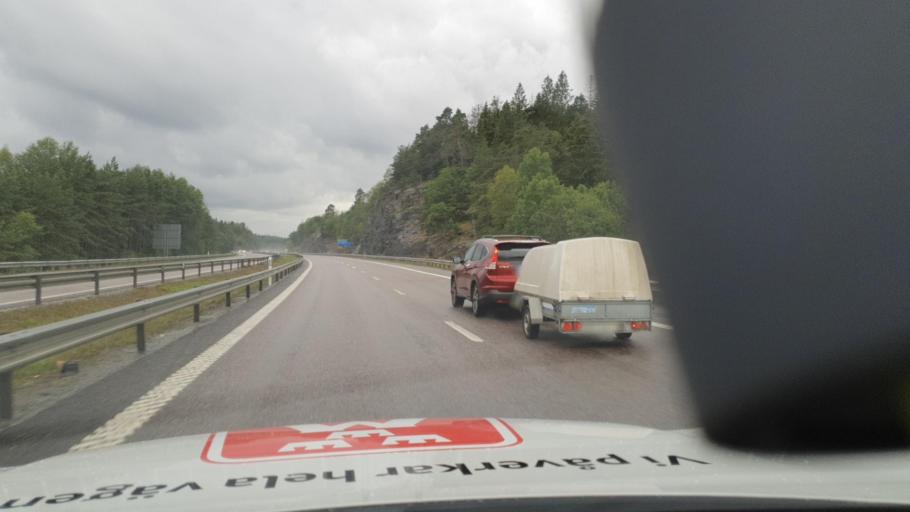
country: SE
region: Vaestra Goetaland
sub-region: Harryda Kommun
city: Landvetter
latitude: 57.6857
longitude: 12.2686
